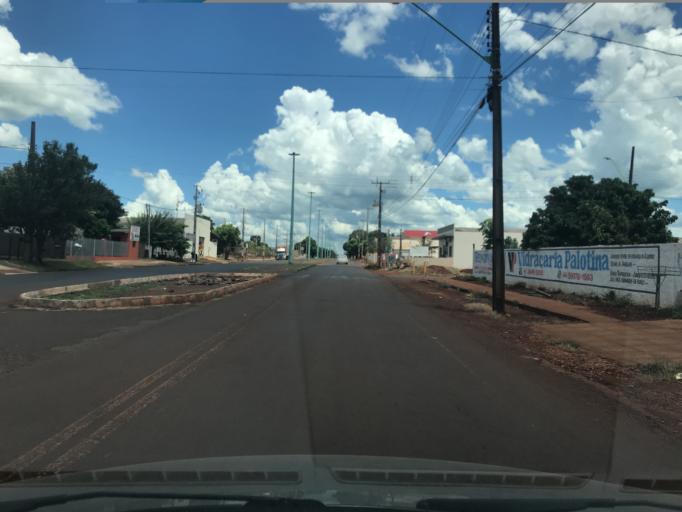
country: BR
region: Parana
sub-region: Palotina
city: Palotina
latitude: -24.2695
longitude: -53.8417
